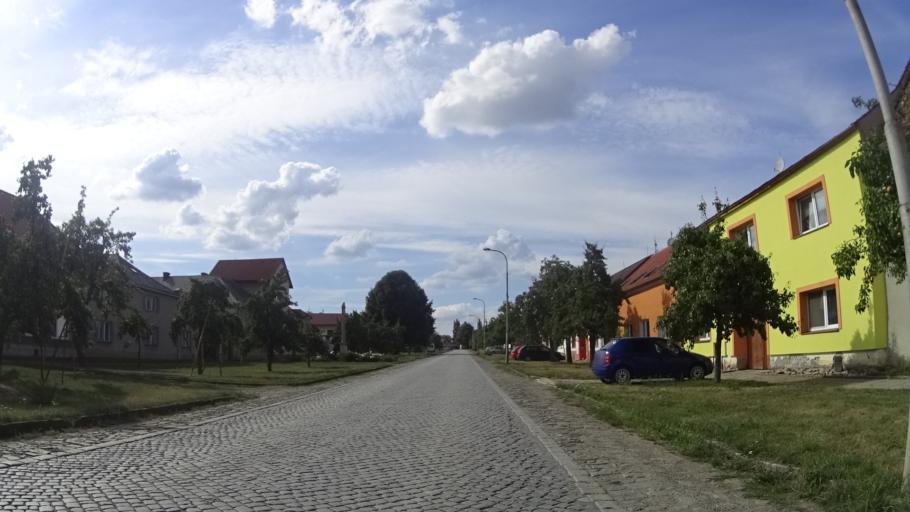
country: CZ
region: Olomoucky
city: Moravicany
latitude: 49.7564
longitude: 16.9611
